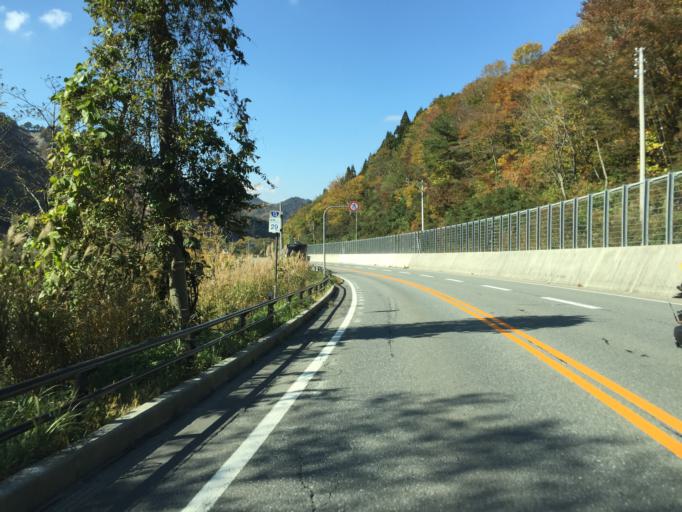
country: JP
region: Yamagata
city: Yonezawa
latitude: 37.8502
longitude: 140.2428
